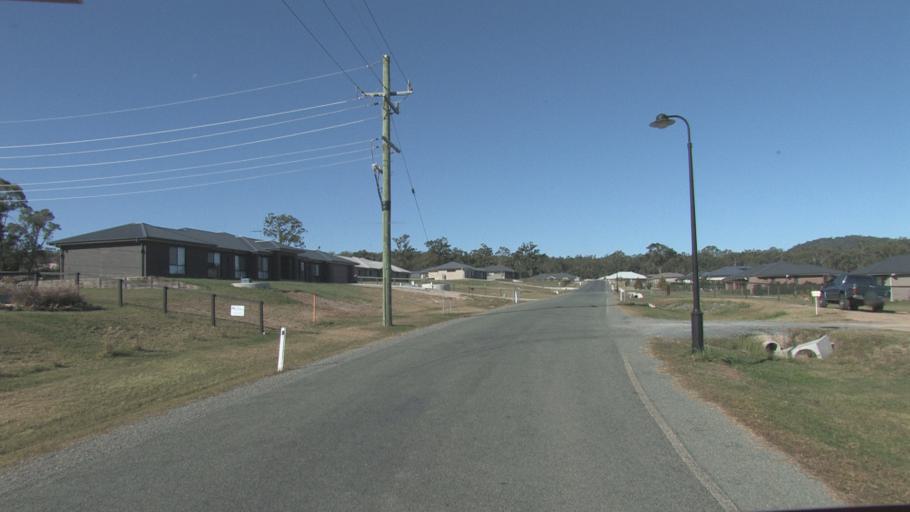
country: AU
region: Queensland
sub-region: Logan
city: Logan Reserve
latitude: -27.7487
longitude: 153.1377
